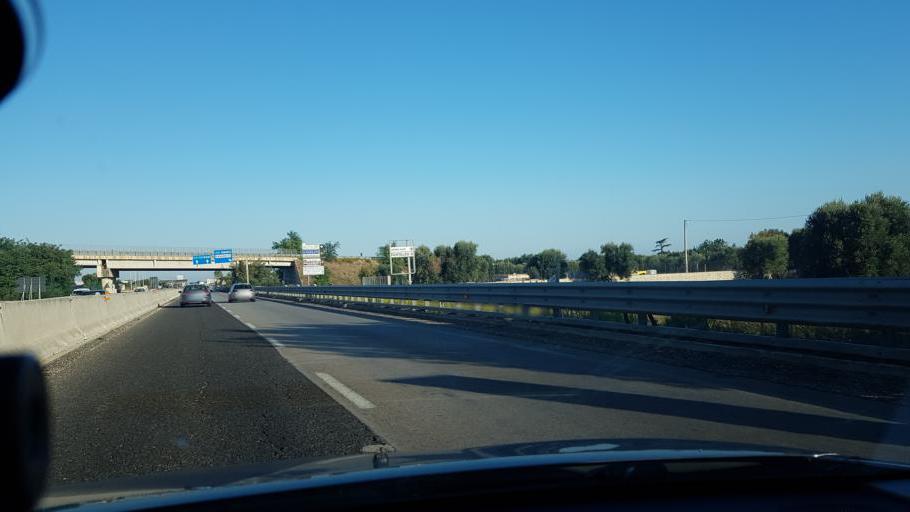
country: IT
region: Apulia
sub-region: Provincia di Brindisi
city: Fasano
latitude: 40.8496
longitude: 17.3590
